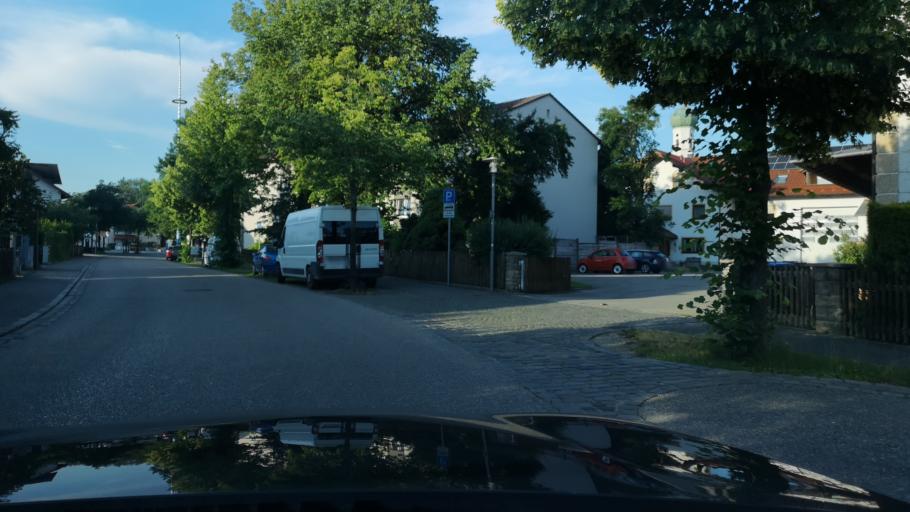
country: DE
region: Bavaria
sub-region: Upper Bavaria
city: Kirchheim bei Muenchen
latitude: 48.1780
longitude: 11.7561
